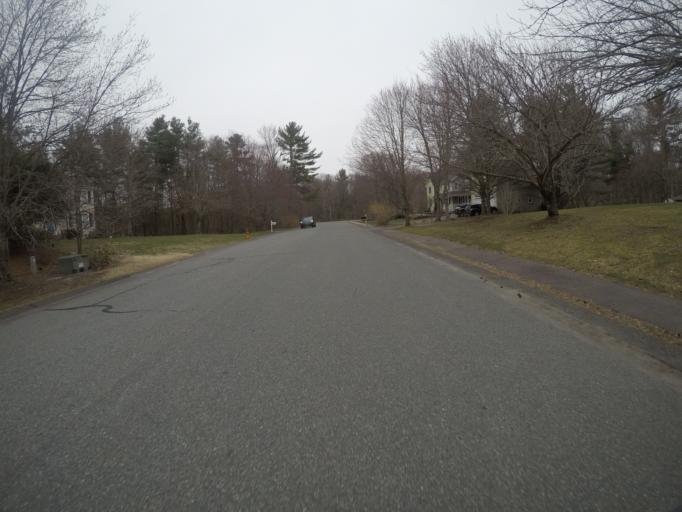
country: US
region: Massachusetts
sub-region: Bristol County
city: Easton
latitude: 42.0312
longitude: -71.1346
